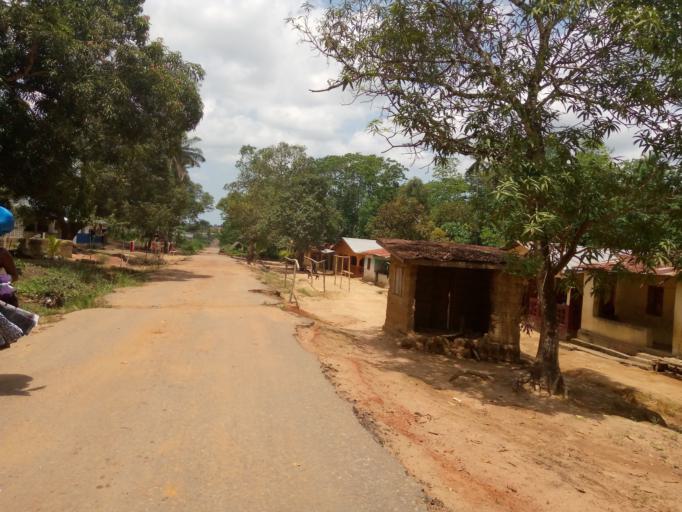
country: SL
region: Western Area
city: Waterloo
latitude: 8.3780
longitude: -12.9595
